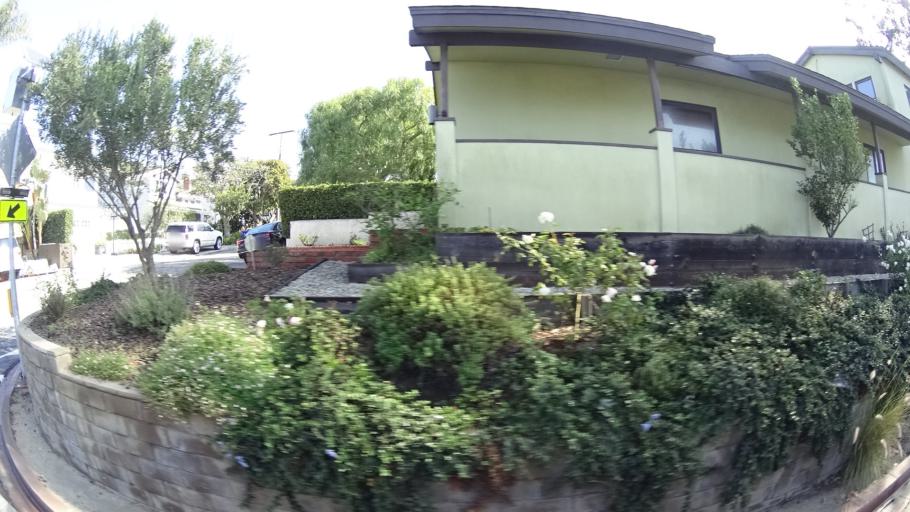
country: US
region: California
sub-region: Los Angeles County
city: Manhattan Beach
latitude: 33.8969
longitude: -118.4097
